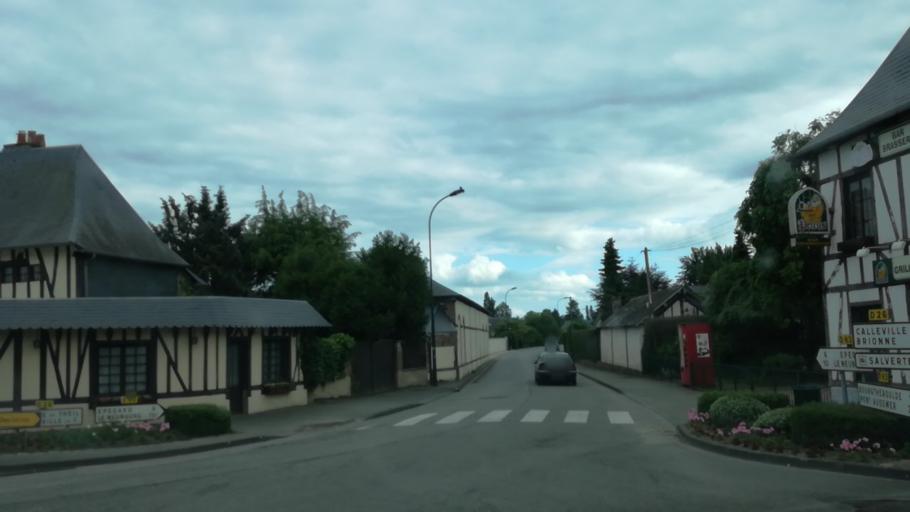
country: FR
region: Haute-Normandie
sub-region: Departement de l'Eure
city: Bourgtheroulde-Infreville
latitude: 49.2263
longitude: 0.8415
